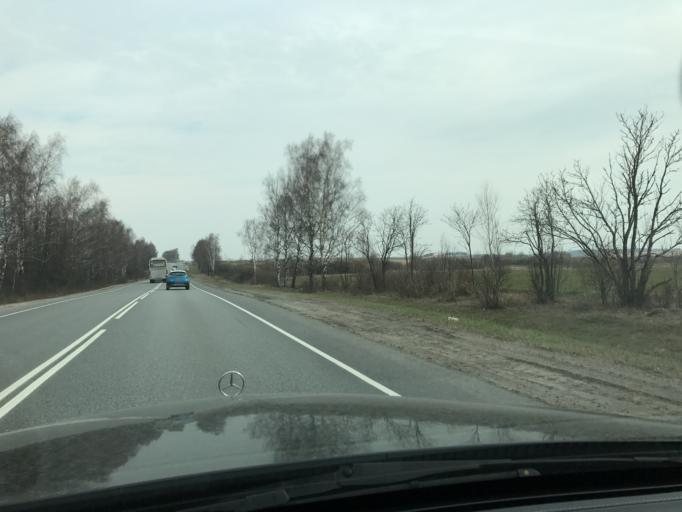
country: RU
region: Vladimir
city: Bogolyubovo
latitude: 56.2940
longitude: 40.4691
